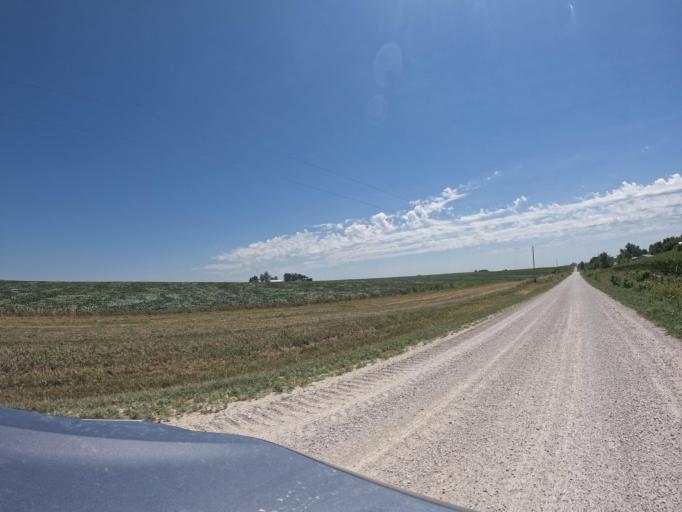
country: US
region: Iowa
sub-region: Keokuk County
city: Sigourney
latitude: 41.4117
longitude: -92.3164
